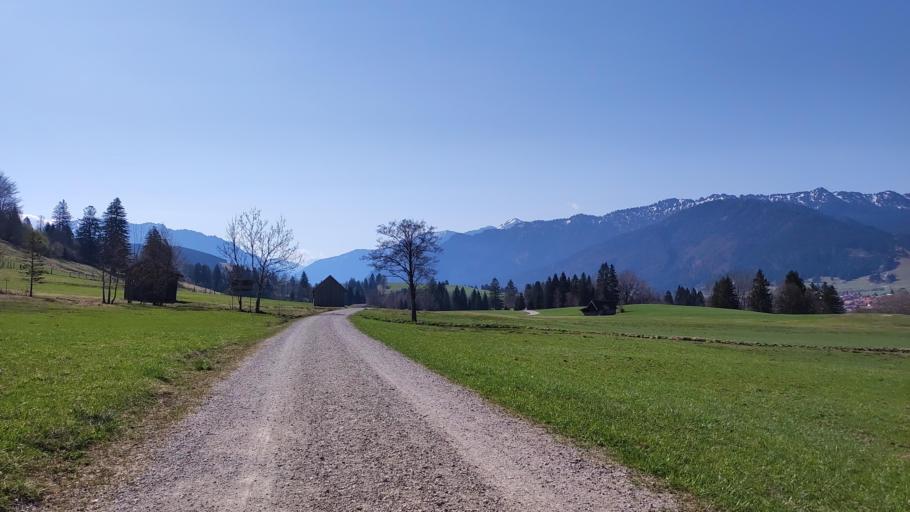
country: DE
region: Bavaria
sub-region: Upper Bavaria
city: Unterammergau
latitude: 47.6344
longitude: 11.0347
